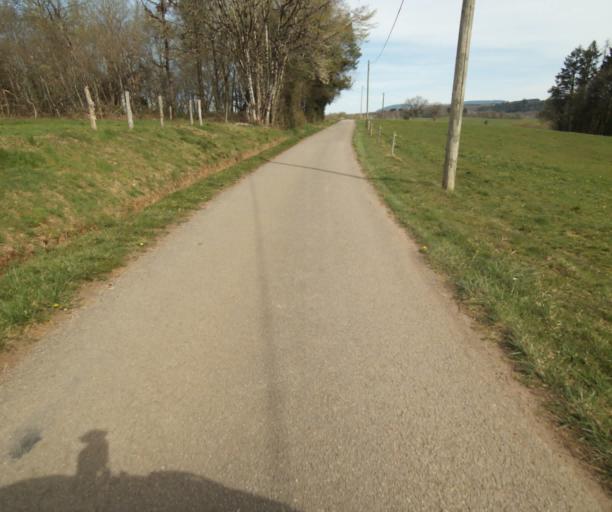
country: FR
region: Limousin
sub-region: Departement de la Correze
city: Correze
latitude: 45.3715
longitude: 1.8195
